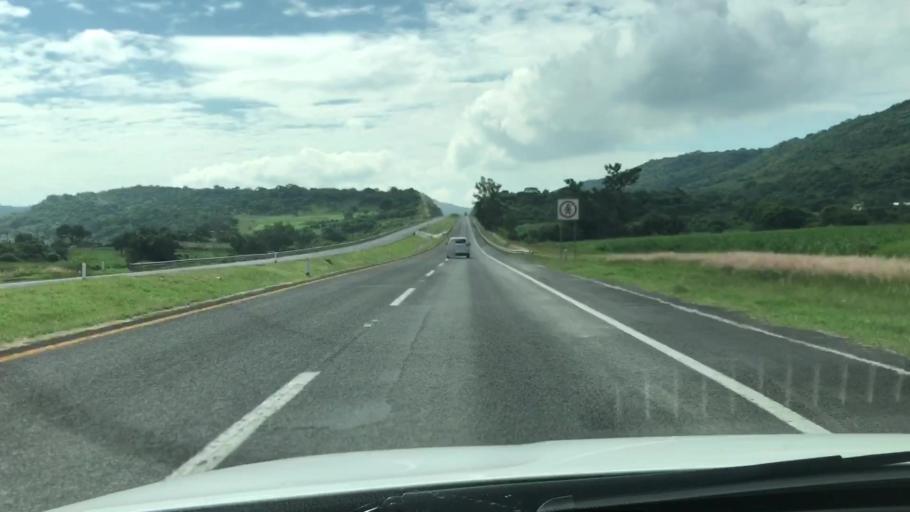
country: MX
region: Jalisco
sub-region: Zapotlanejo
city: La Mezquitera
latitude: 20.5389
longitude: -103.0213
